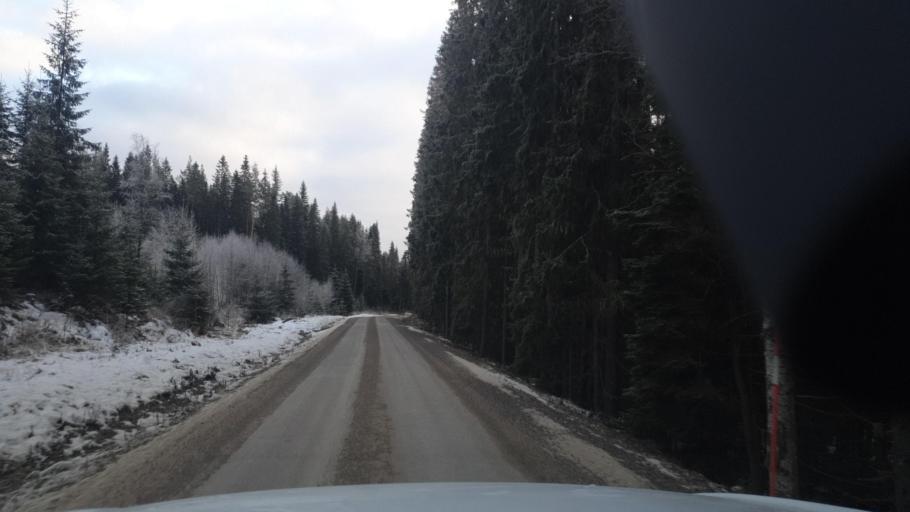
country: SE
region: Vaermland
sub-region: Eda Kommun
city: Charlottenberg
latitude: 60.0379
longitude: 12.5880
